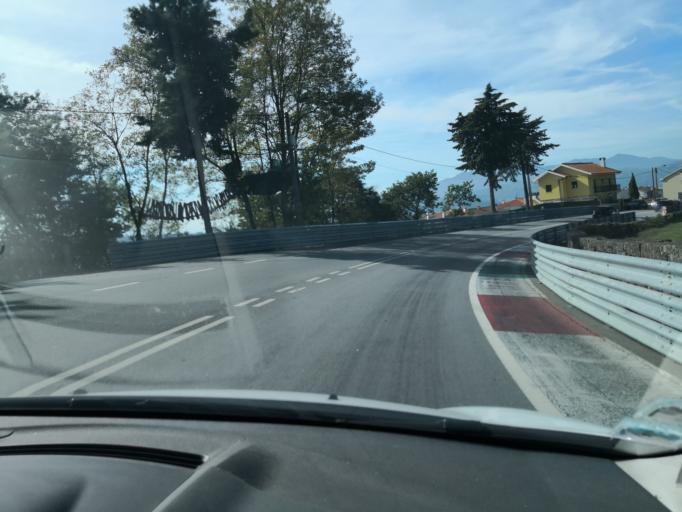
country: PT
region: Vila Real
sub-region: Vila Real
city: Vila Real
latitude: 41.2974
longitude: -7.7179
